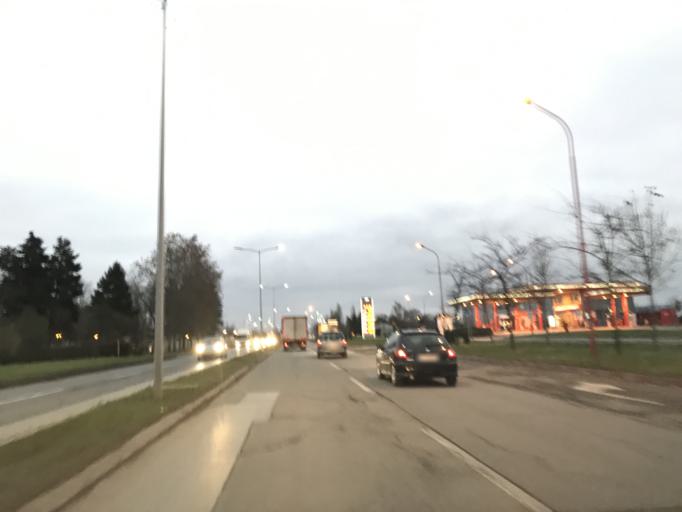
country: RS
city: Veternik
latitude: 45.2767
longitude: 19.7980
